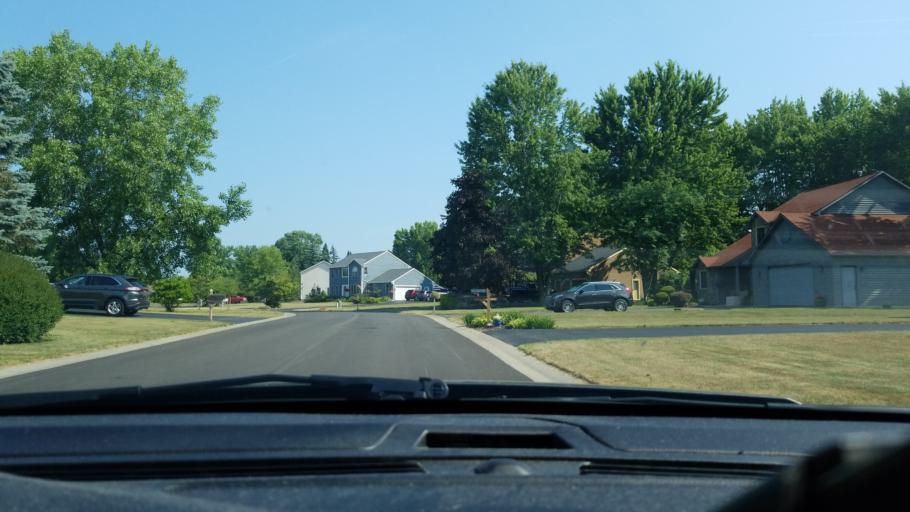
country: US
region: New York
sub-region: Onondaga County
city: East Syracuse
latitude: 43.0971
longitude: -76.0706
